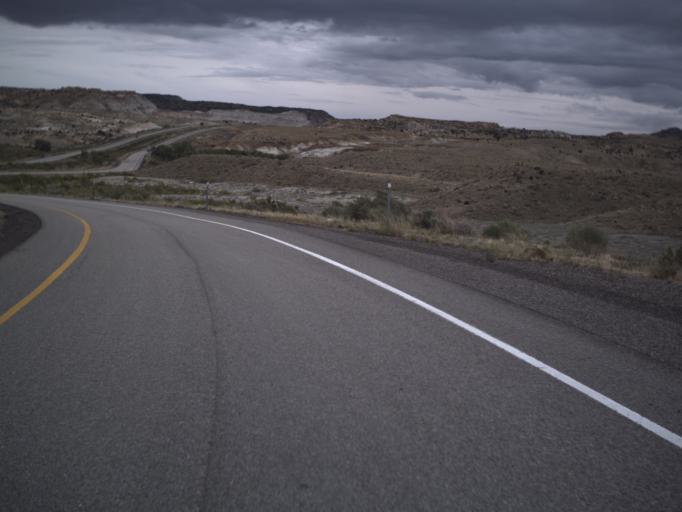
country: US
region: Utah
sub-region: Emery County
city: Ferron
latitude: 38.8101
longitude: -111.2093
